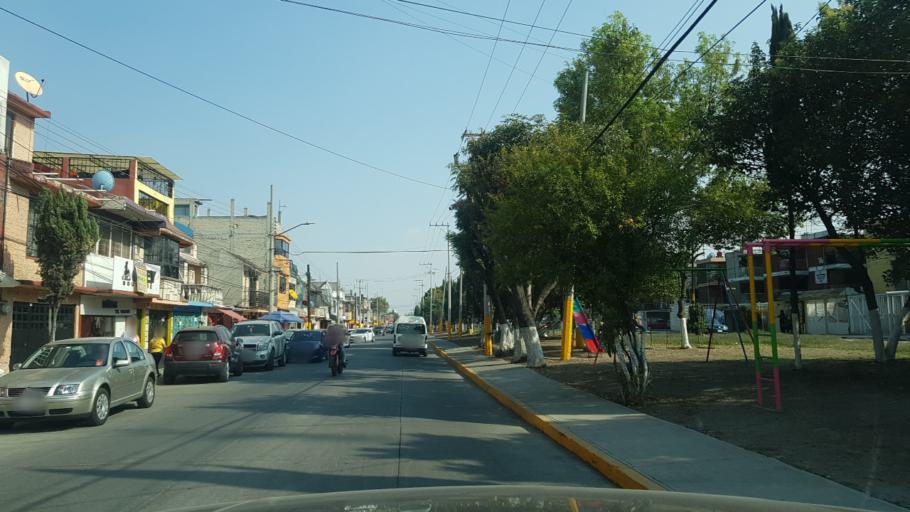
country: MX
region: Mexico
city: Santiago Teyahualco
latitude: 19.6526
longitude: -99.1187
